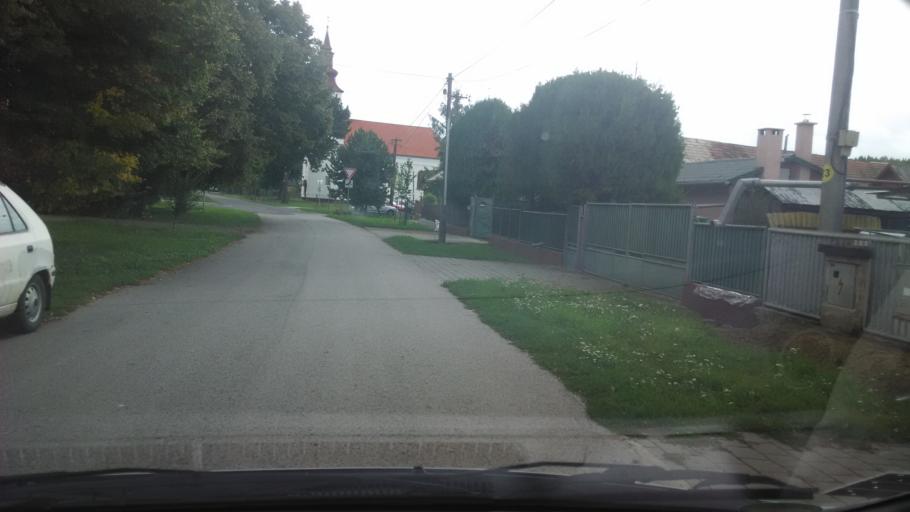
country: SK
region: Nitriansky
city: Levice
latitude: 48.1958
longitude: 18.5226
